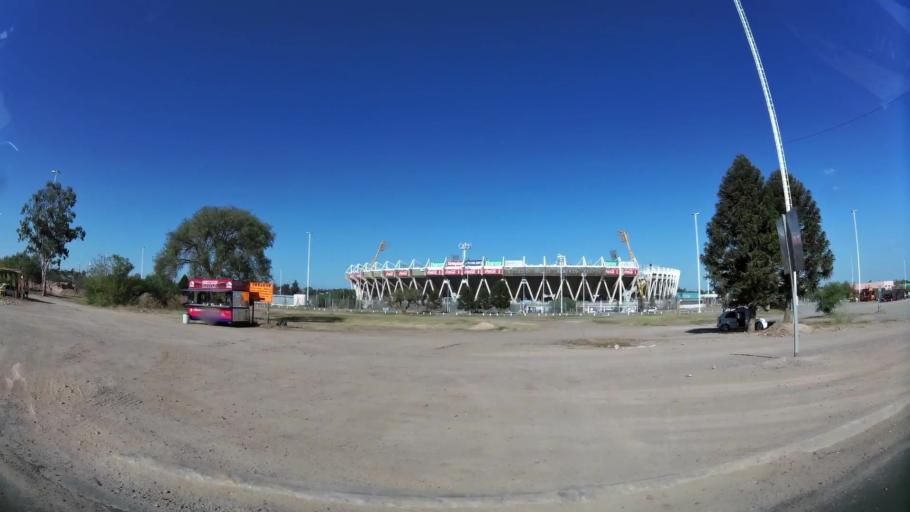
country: AR
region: Cordoba
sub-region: Departamento de Capital
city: Cordoba
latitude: -31.3685
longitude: -64.2501
